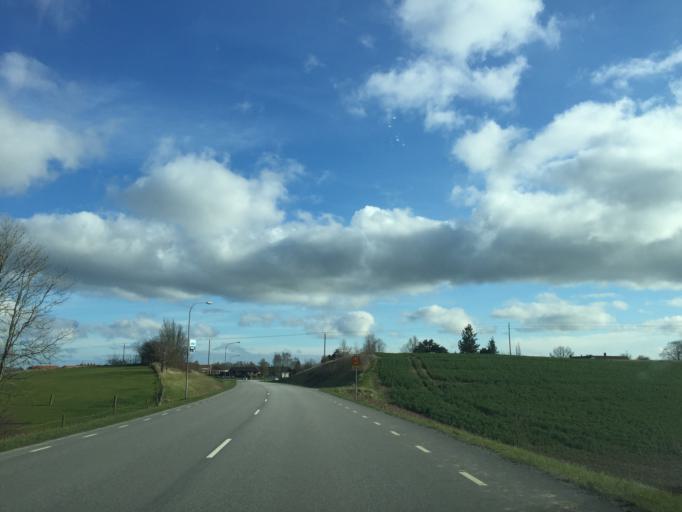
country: SE
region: Skane
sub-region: Skurups Kommun
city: Rydsgard
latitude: 55.4799
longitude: 13.5933
